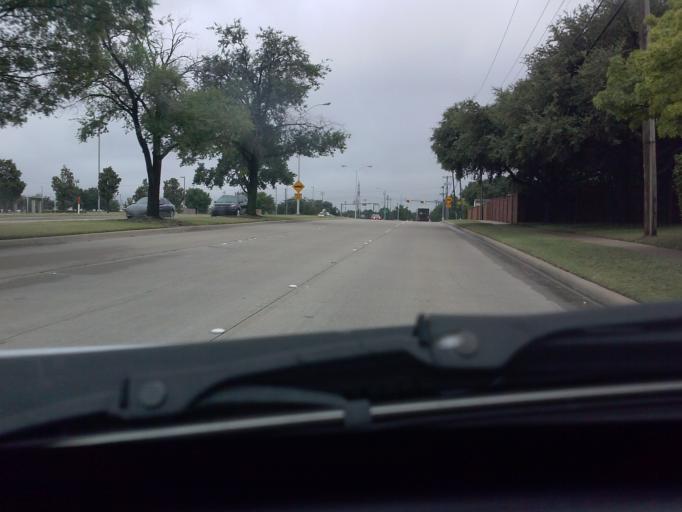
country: US
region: Texas
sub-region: Collin County
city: Plano
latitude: 33.0672
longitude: -96.7097
